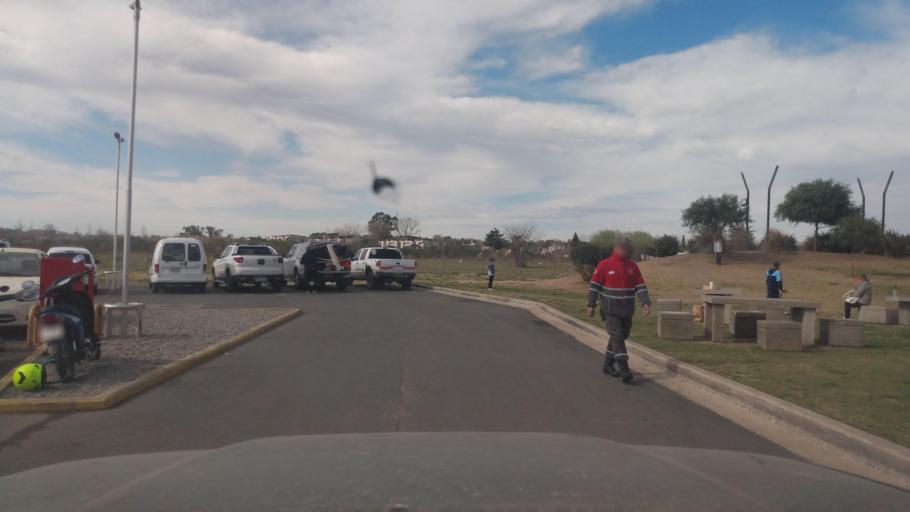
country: AR
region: Buenos Aires
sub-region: Partido de Lujan
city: Lujan
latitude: -34.5462
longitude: -59.1095
